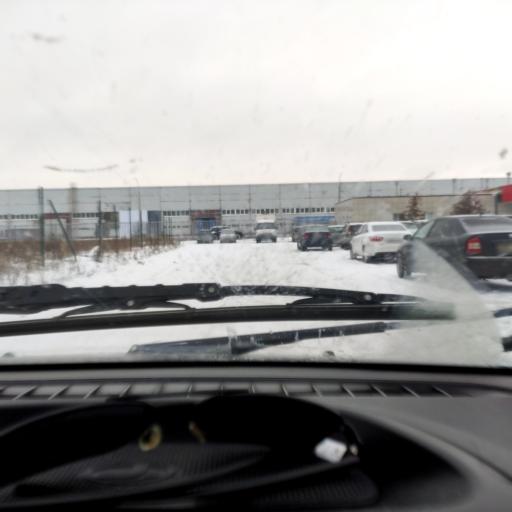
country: RU
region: Samara
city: Zhigulevsk
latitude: 53.5158
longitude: 49.5272
